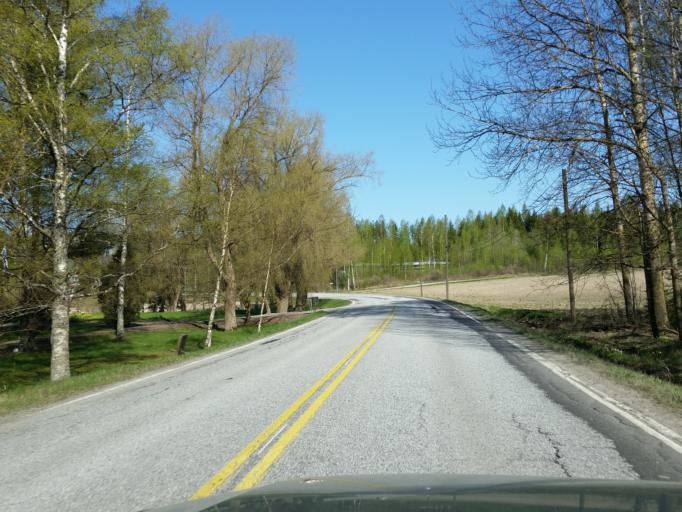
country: FI
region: Uusimaa
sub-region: Helsinki
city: Lohja
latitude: 60.1747
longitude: 24.0934
